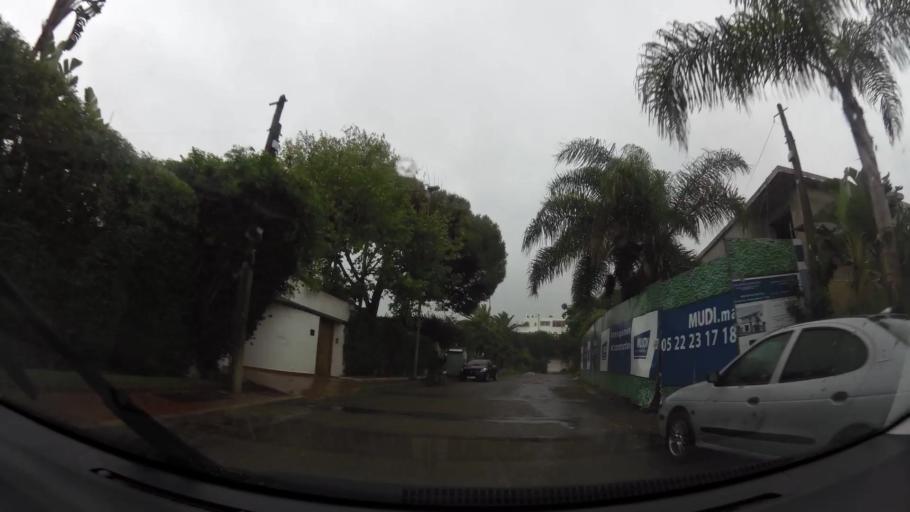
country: MA
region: Grand Casablanca
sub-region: Casablanca
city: Casablanca
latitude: 33.5862
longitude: -7.6762
